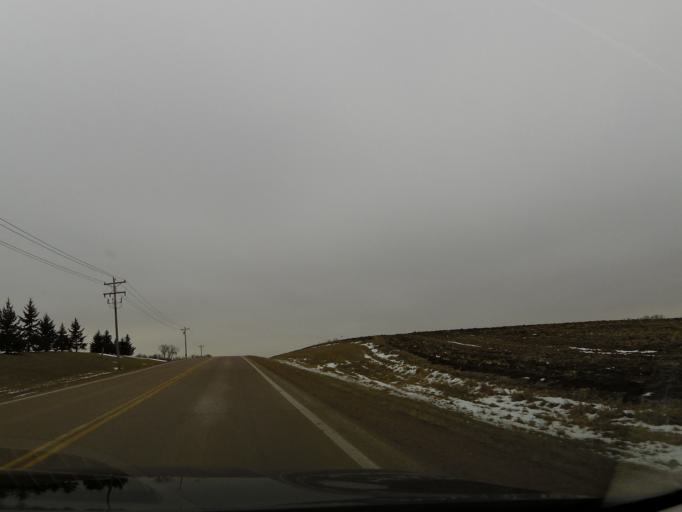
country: US
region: Minnesota
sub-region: Carver County
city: Carver
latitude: 44.7730
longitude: -93.6838
